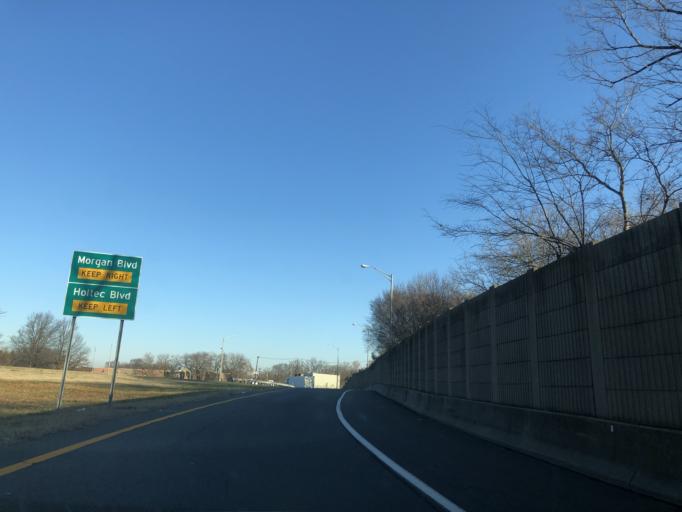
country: US
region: New Jersey
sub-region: Camden County
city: Camden
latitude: 39.9109
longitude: -75.1151
